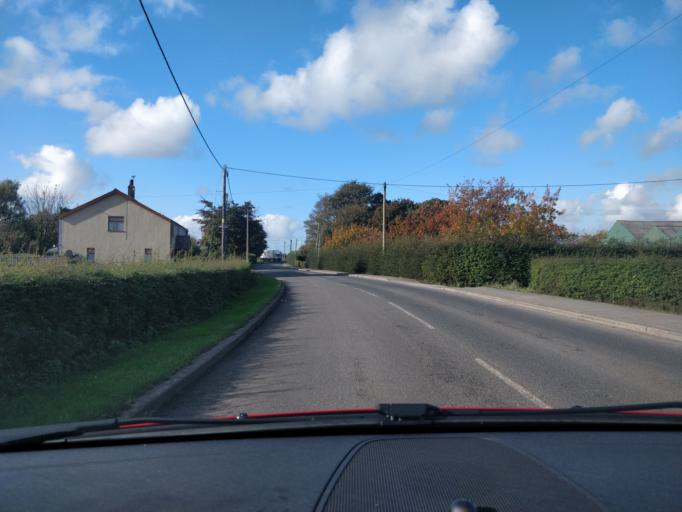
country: GB
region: England
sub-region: Lancashire
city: Banks
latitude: 53.6961
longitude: -2.8848
